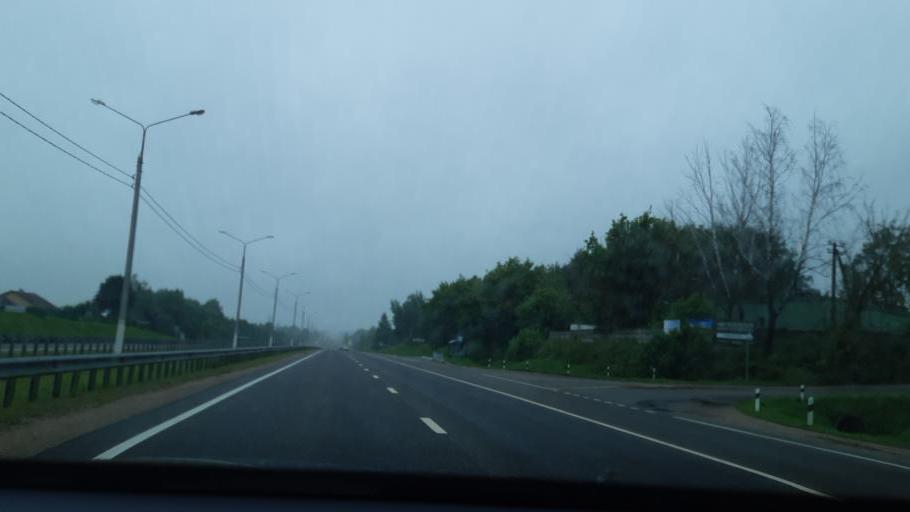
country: RU
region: Smolensk
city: Talashkino
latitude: 54.6496
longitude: 32.1690
